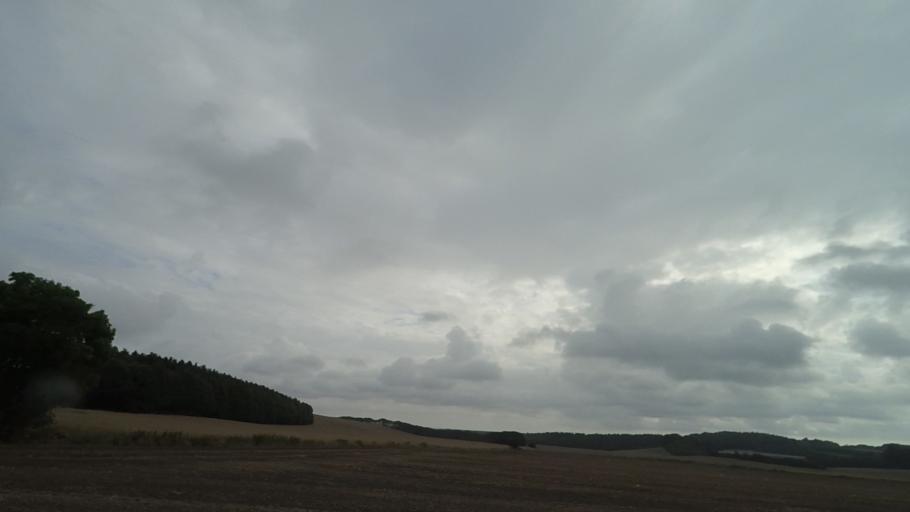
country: DK
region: Central Jutland
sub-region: Syddjurs Kommune
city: Ronde
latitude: 56.3303
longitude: 10.4581
